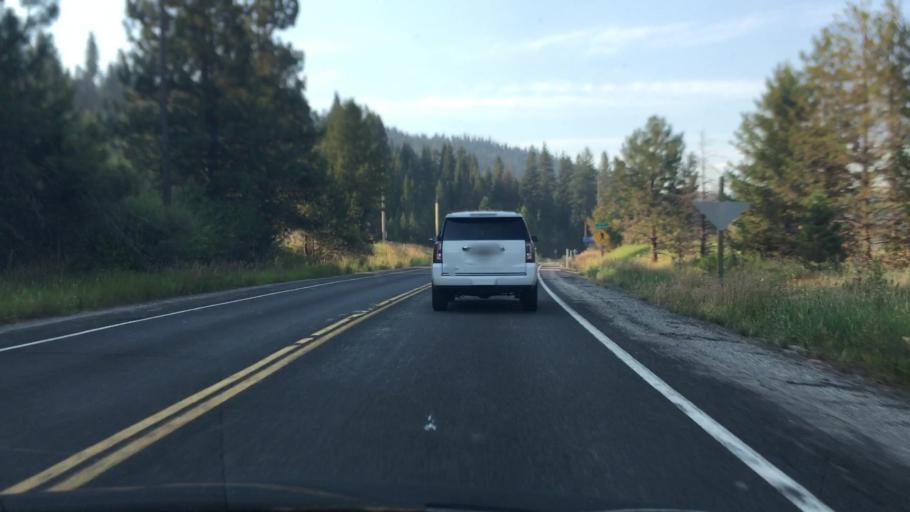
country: US
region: Idaho
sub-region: Valley County
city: Cascade
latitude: 44.2998
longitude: -116.0890
